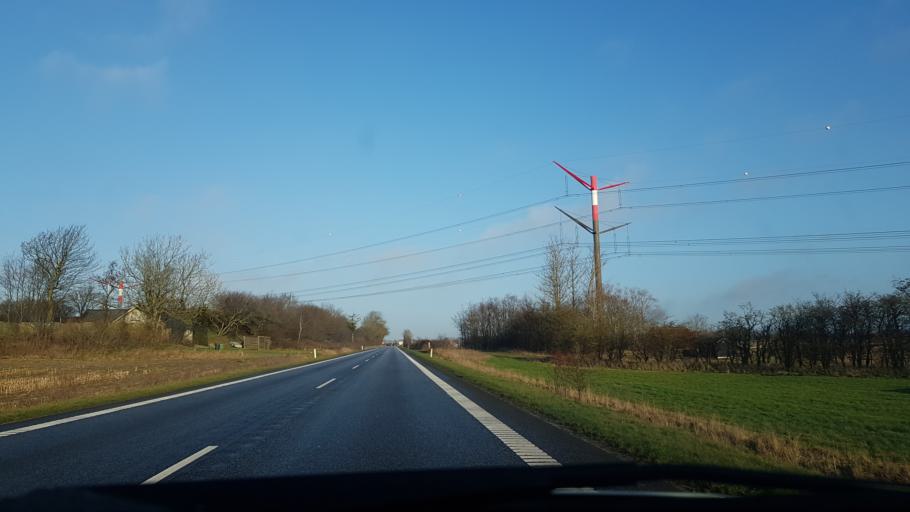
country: DK
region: South Denmark
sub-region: Tonder Kommune
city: Toftlund
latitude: 55.2484
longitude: 9.1392
